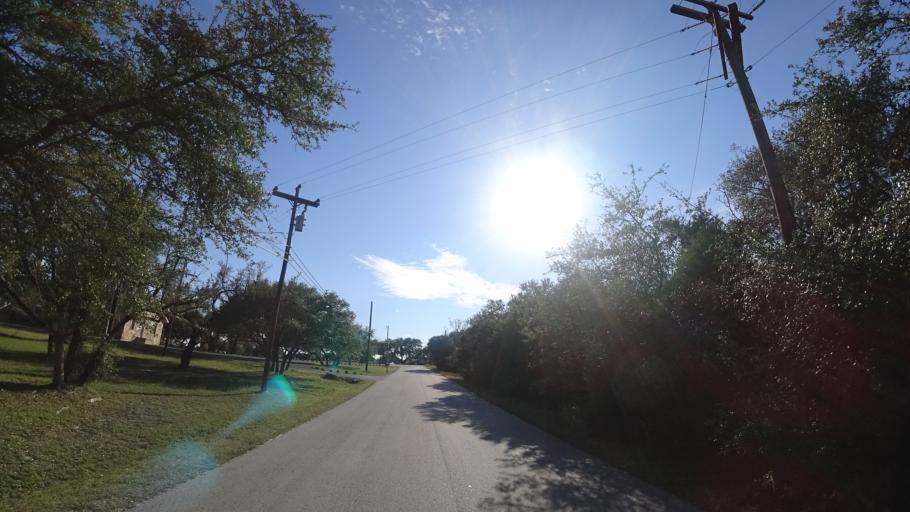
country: US
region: Texas
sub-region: Travis County
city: Barton Creek
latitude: 30.2360
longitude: -97.9108
